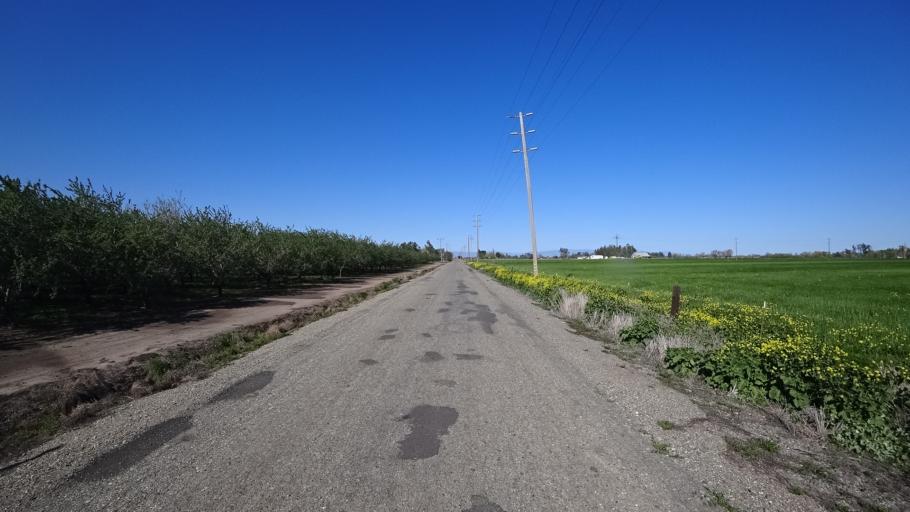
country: US
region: California
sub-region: Glenn County
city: Hamilton City
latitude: 39.7756
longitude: -122.0501
